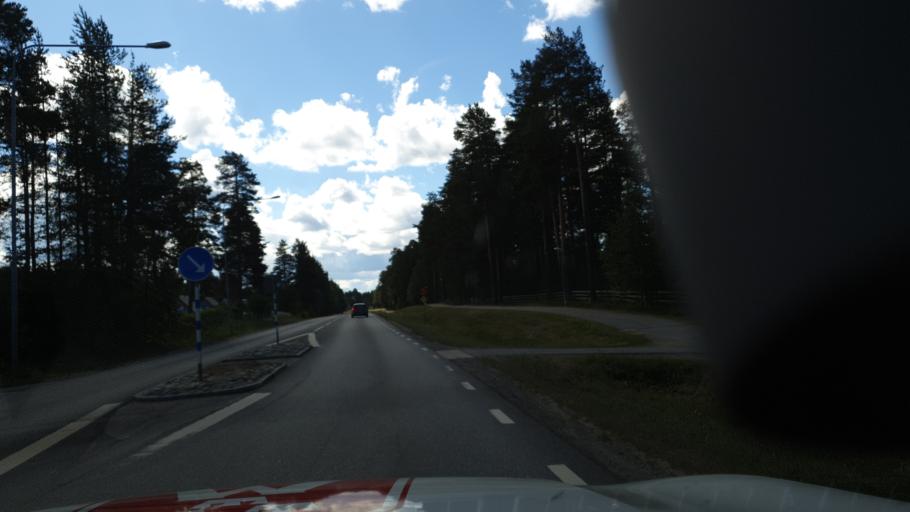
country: SE
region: Vaesterbotten
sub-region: Lycksele Kommun
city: Lycksele
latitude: 64.6004
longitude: 18.7009
